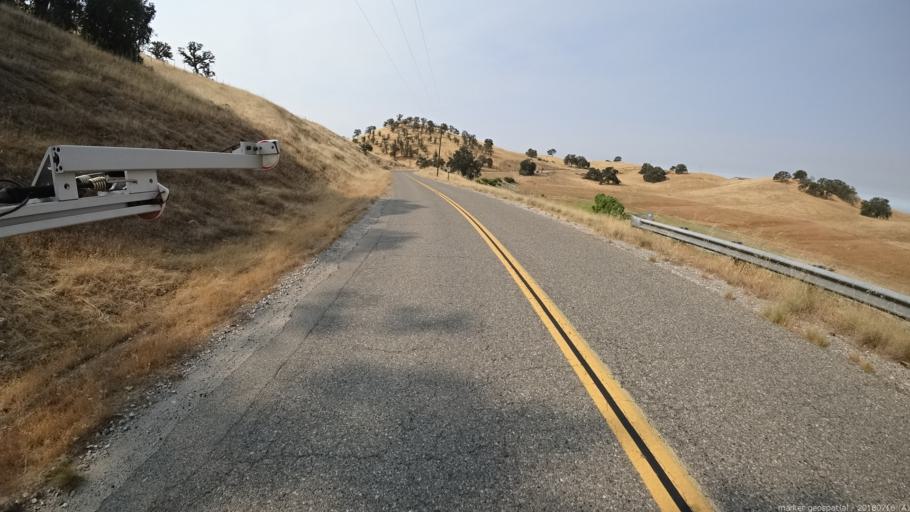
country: US
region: California
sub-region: Madera County
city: Bonadelle Ranchos-Madera Ranchos
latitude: 37.1057
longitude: -119.8680
